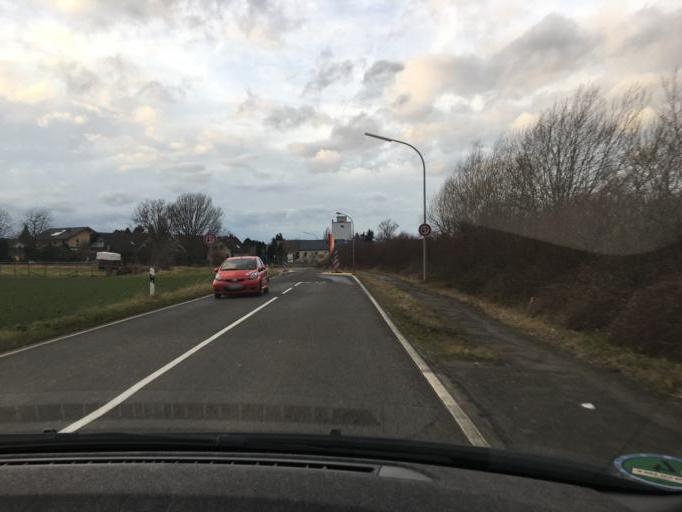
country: DE
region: North Rhine-Westphalia
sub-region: Regierungsbezirk Koln
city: Bad Munstereifel
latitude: 50.6038
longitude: 6.7453
